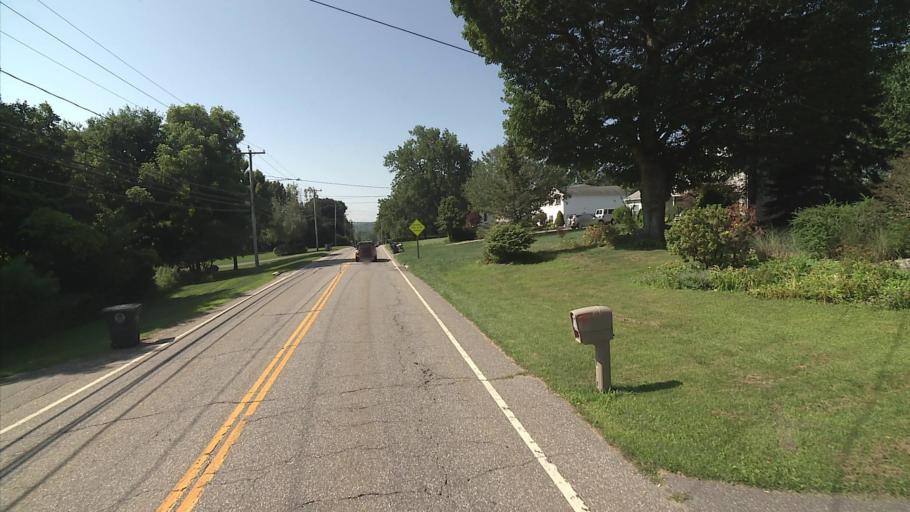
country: US
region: Connecticut
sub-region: Litchfield County
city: Torrington
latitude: 41.8246
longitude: -73.0800
